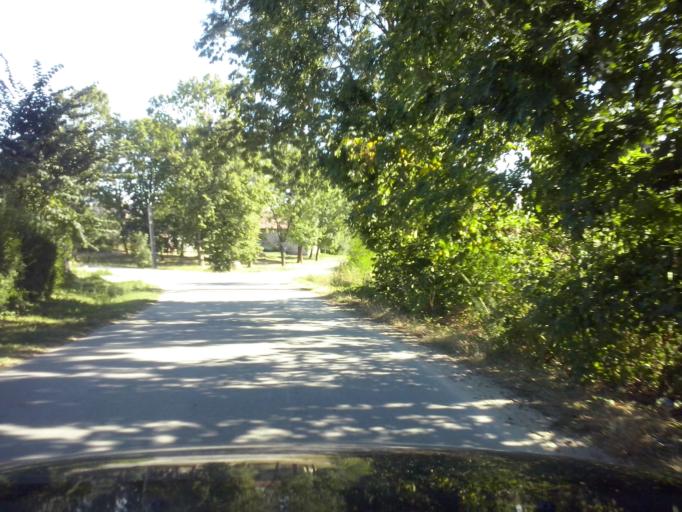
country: PL
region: Swietokrzyskie
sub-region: Powiat pinczowski
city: Kije
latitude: 50.5802
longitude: 20.6549
